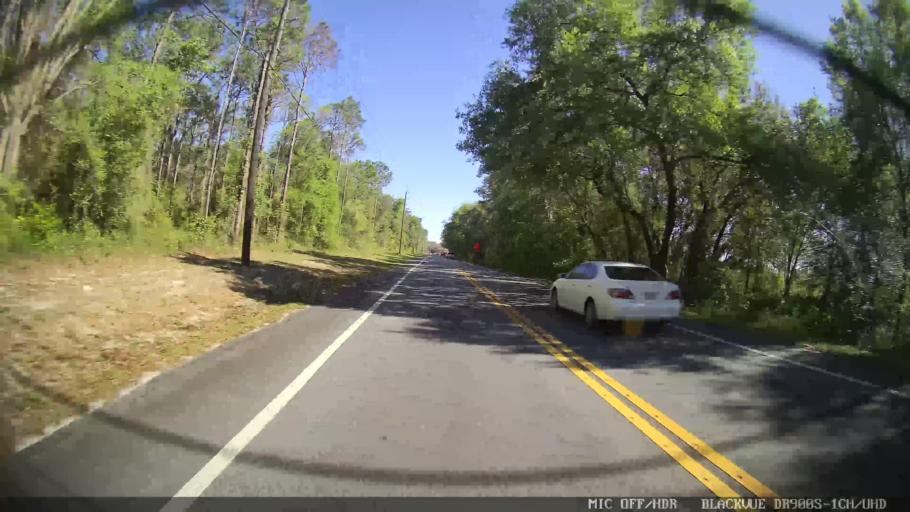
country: US
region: Florida
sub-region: Pasco County
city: Shady Hills
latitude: 28.3339
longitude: -82.5444
